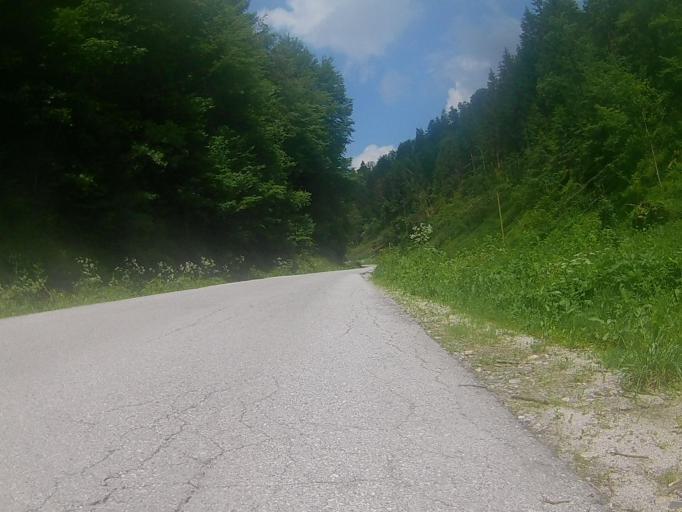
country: SI
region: Maribor
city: Bresternica
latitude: 46.6006
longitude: 15.5546
